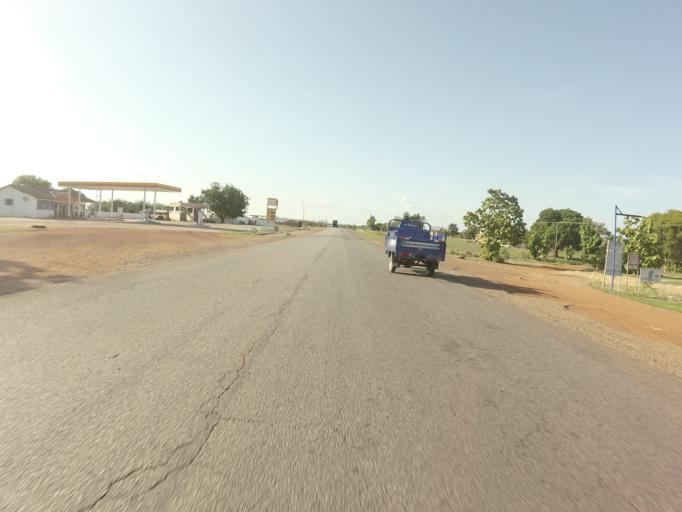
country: GH
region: Upper East
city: Navrongo
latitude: 10.9225
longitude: -1.0893
